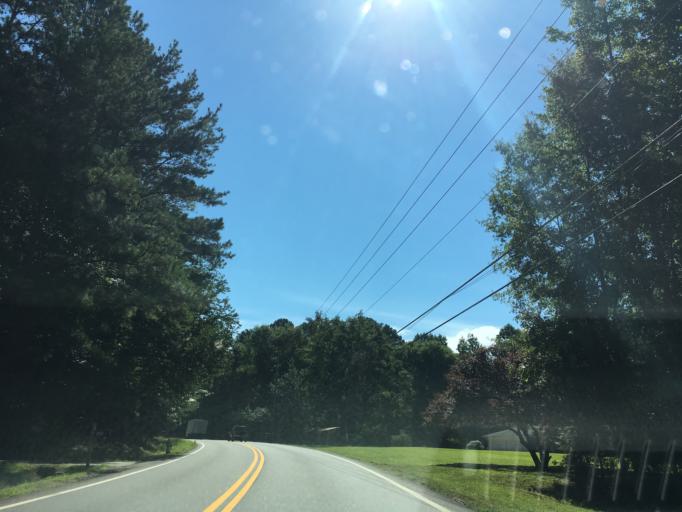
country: US
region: Georgia
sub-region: Fulton County
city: Milton
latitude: 34.1635
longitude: -84.2984
